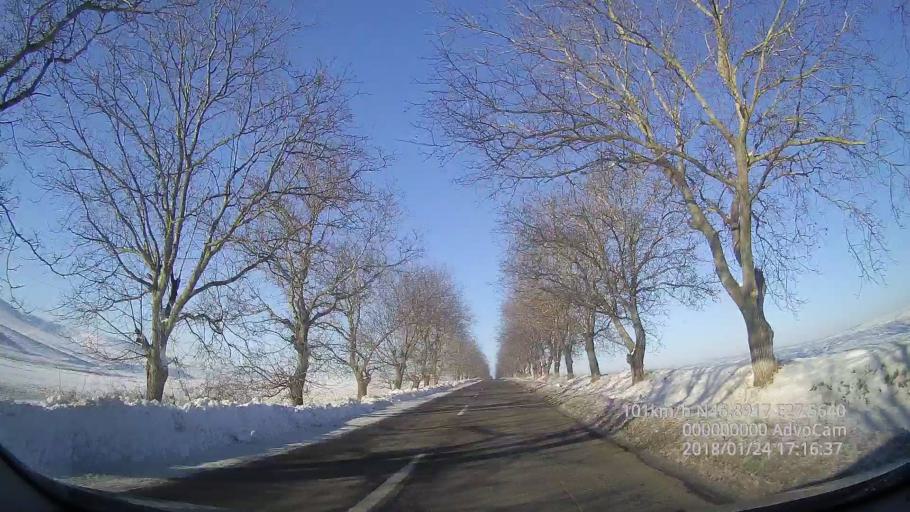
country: RO
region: Iasi
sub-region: Comuna Scanteia
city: Scanteia
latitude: 46.8926
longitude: 27.5640
